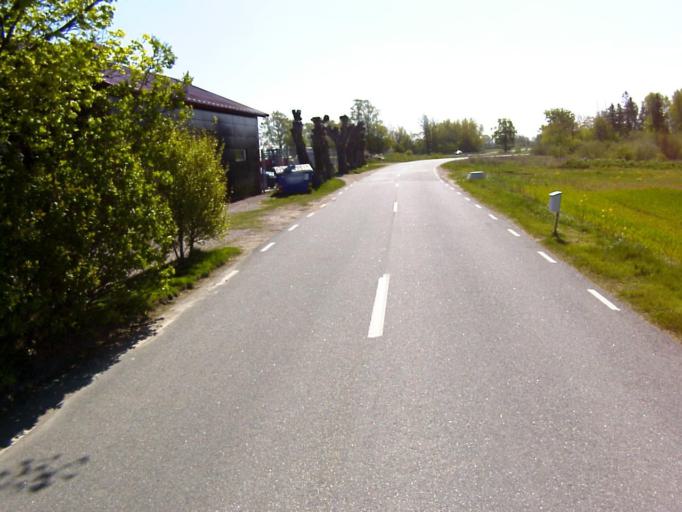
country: SE
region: Skane
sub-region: Kristianstads Kommun
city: Fjalkinge
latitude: 56.0073
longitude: 14.2610
